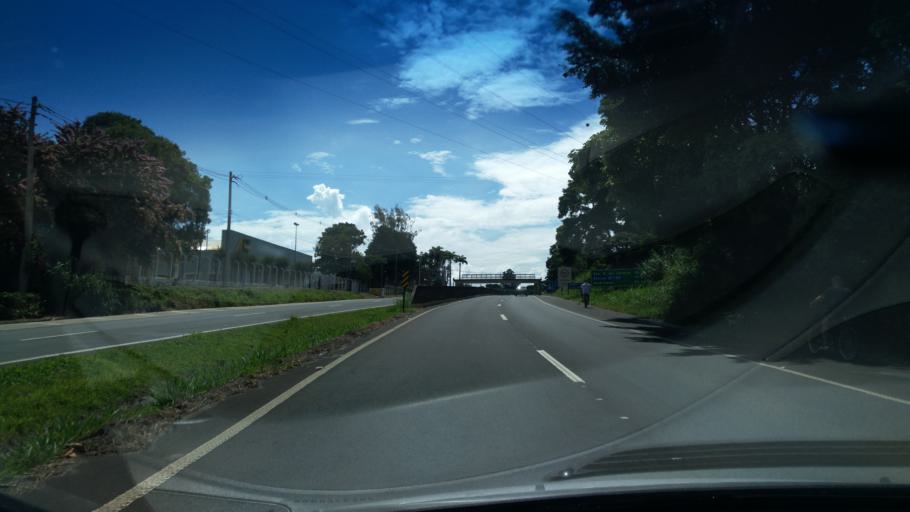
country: BR
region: Sao Paulo
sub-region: Santo Antonio Do Jardim
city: Espirito Santo do Pinhal
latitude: -22.1883
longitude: -46.7666
